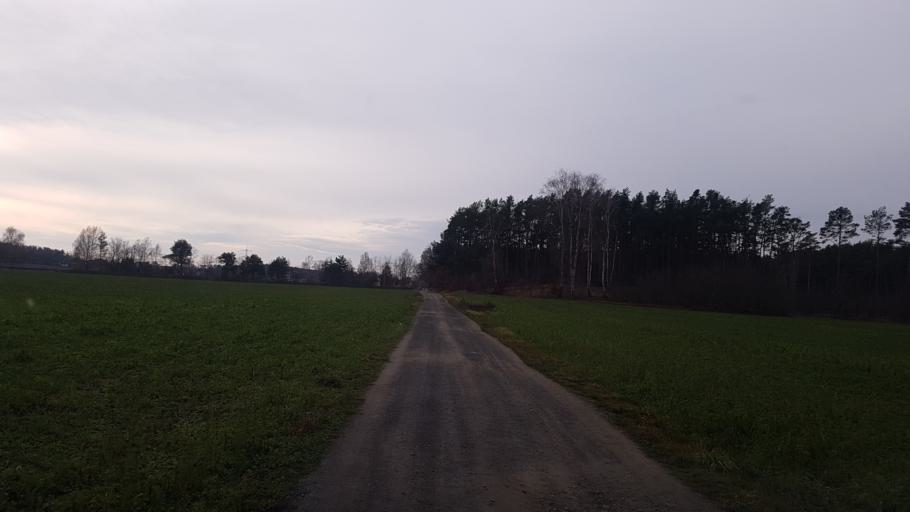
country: DE
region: Brandenburg
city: Schonborn
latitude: 51.5671
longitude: 13.4888
